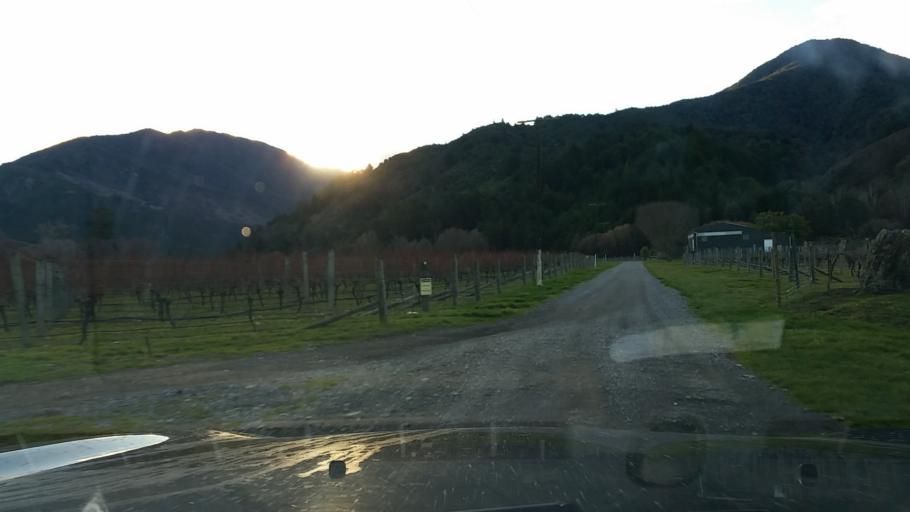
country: NZ
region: Marlborough
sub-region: Marlborough District
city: Blenheim
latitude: -41.5060
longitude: 173.5779
